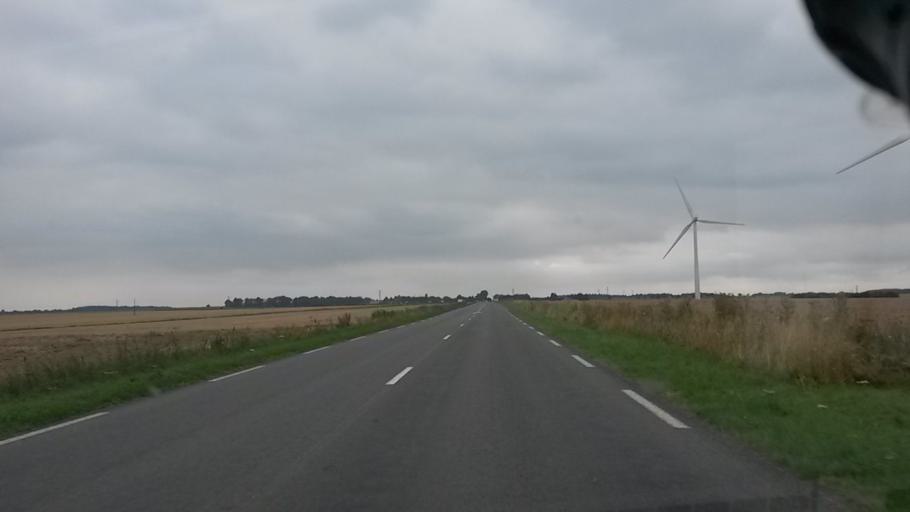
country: FR
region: Haute-Normandie
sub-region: Departement de la Seine-Maritime
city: Aumale
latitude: 49.7699
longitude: 1.8235
